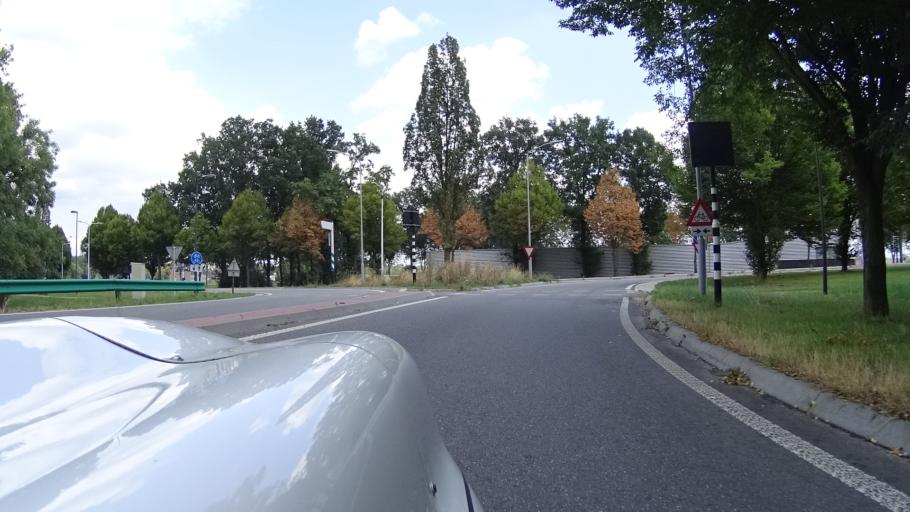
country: NL
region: Gelderland
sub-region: Gemeente Maasdriel
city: Hedel
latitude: 51.7446
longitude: 5.2665
